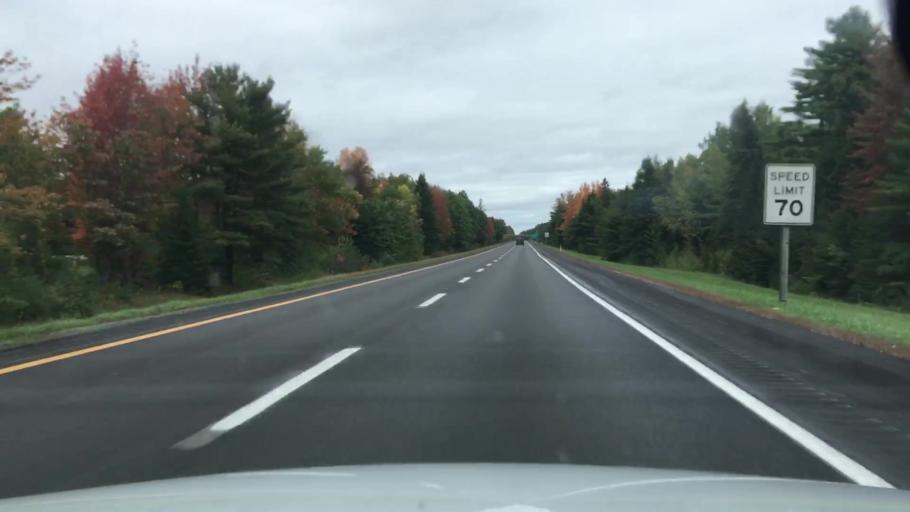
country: US
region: Maine
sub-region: Penobscot County
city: Orono
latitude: 44.8812
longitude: -68.6968
